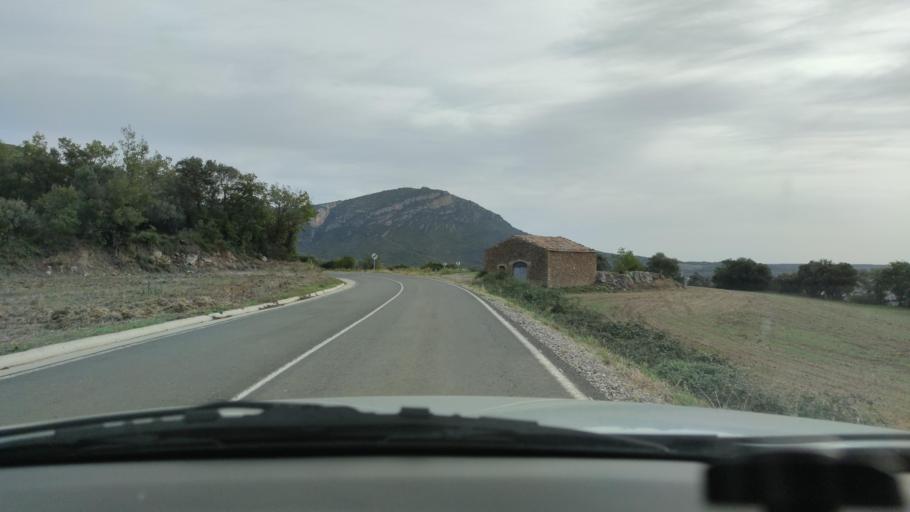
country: ES
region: Catalonia
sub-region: Provincia de Lleida
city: Artesa de Segre
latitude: 41.9914
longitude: 1.0036
